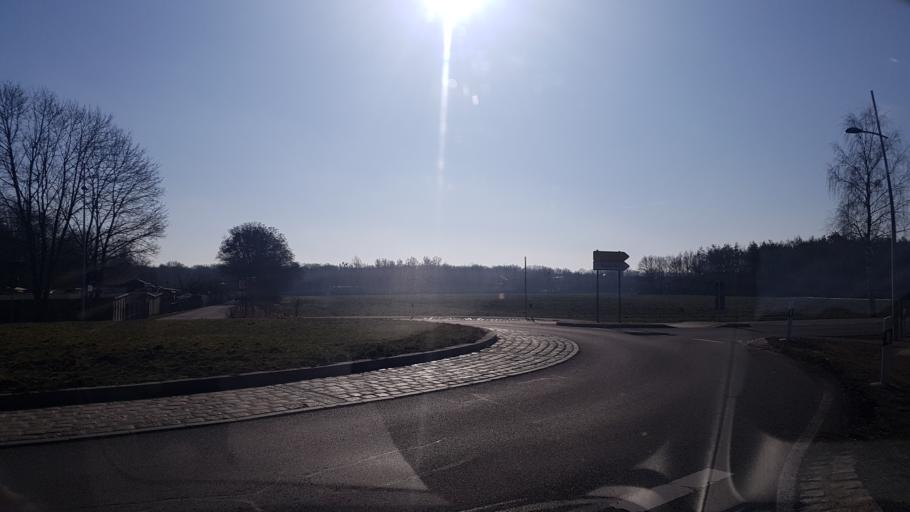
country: DE
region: Brandenburg
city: Senftenberg
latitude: 51.4996
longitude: 13.9616
